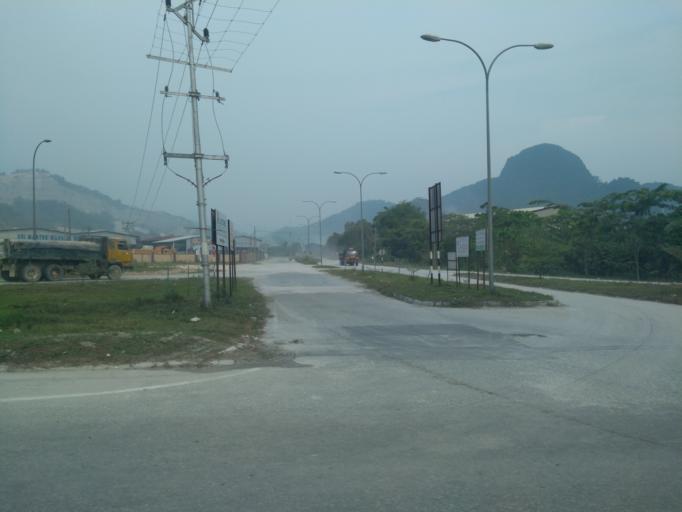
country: MY
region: Perak
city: Ipoh
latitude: 4.5360
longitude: 101.1513
